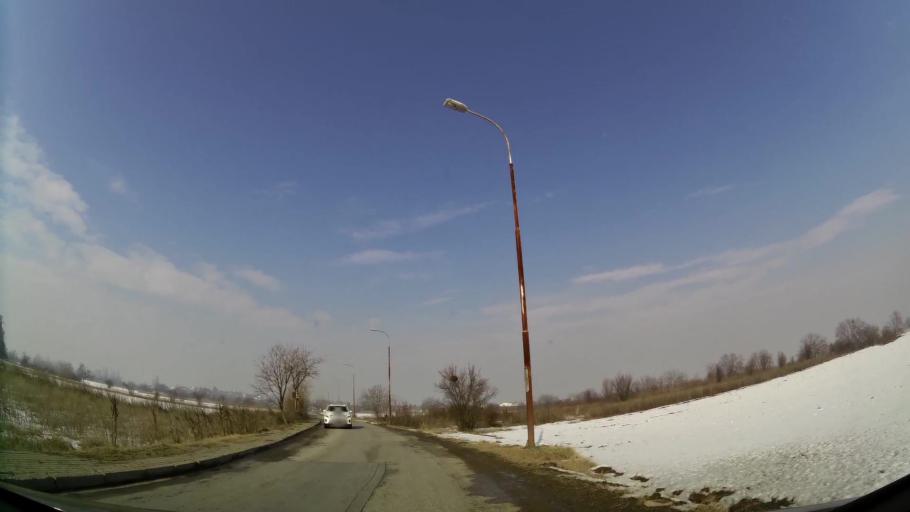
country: MK
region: Suto Orizari
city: Suto Orizare
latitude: 42.0196
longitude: 21.3881
